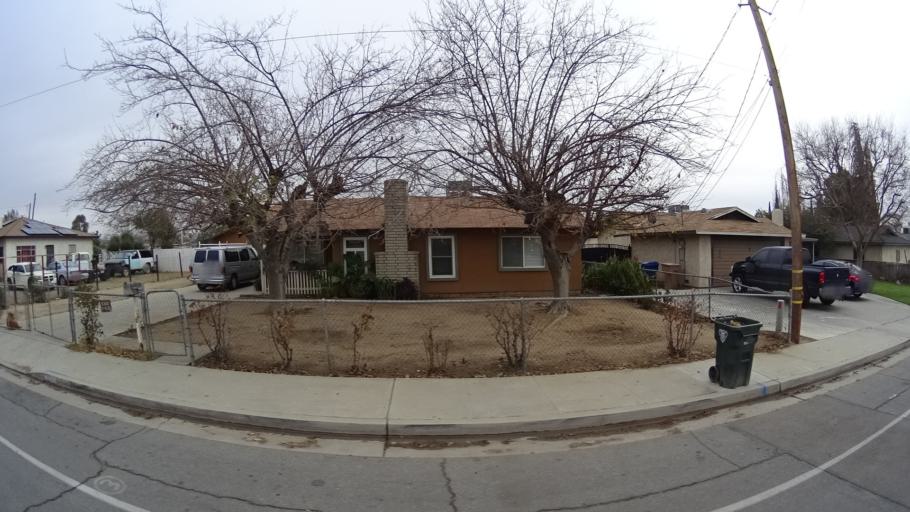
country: US
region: California
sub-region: Kern County
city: Bakersfield
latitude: 35.3627
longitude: -118.9497
